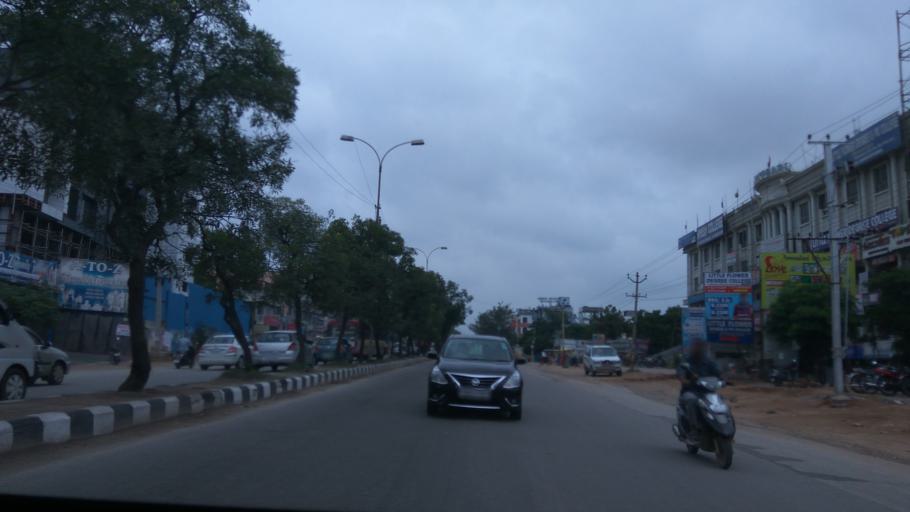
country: IN
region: Telangana
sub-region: Rangareddi
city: Secunderabad
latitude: 17.4779
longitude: 78.5620
